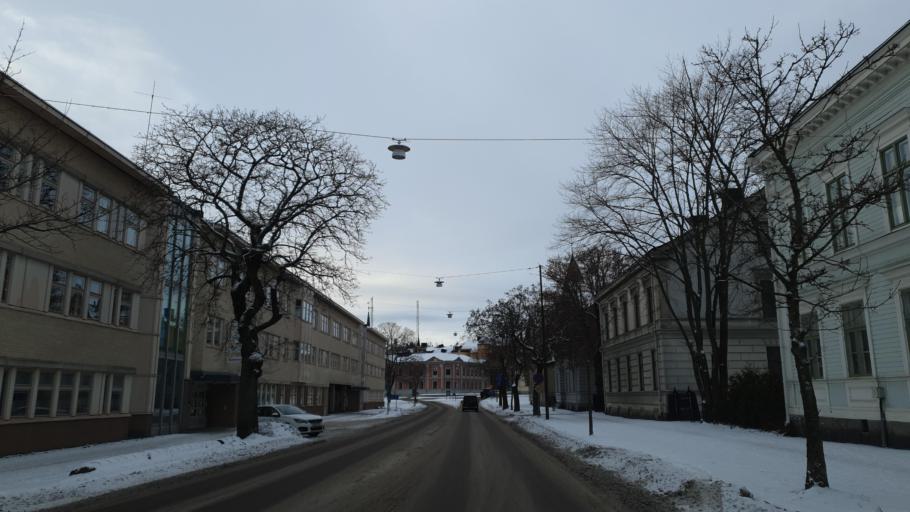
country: SE
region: Gaevleborg
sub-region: Soderhamns Kommun
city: Soderhamn
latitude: 61.3035
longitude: 17.0549
